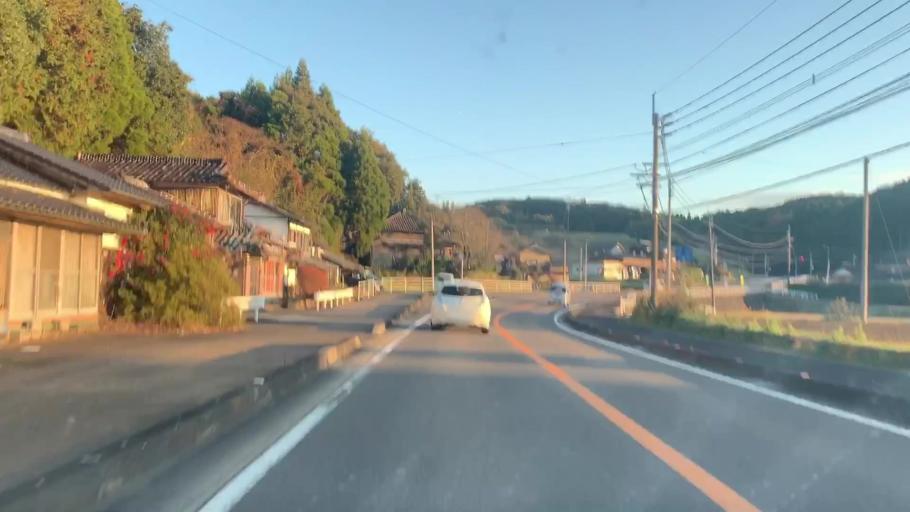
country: JP
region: Saga Prefecture
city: Imaricho-ko
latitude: 33.2661
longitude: 129.9650
